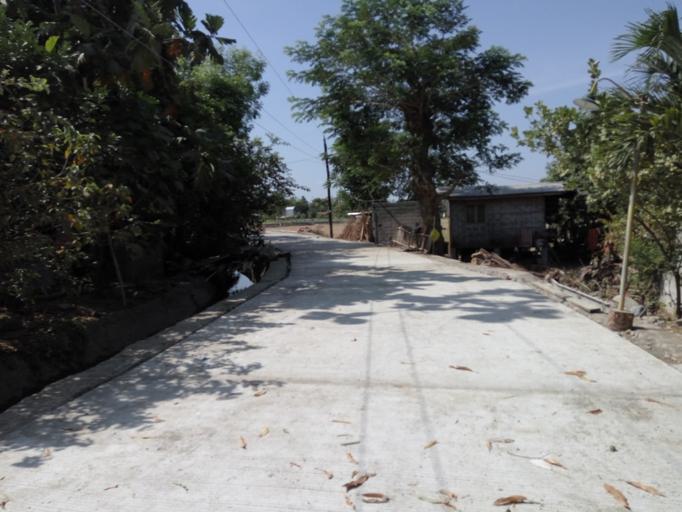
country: PH
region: Ilocos
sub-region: Province of Ilocos Sur
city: Santa Maria
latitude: 16.9464
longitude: 120.4605
